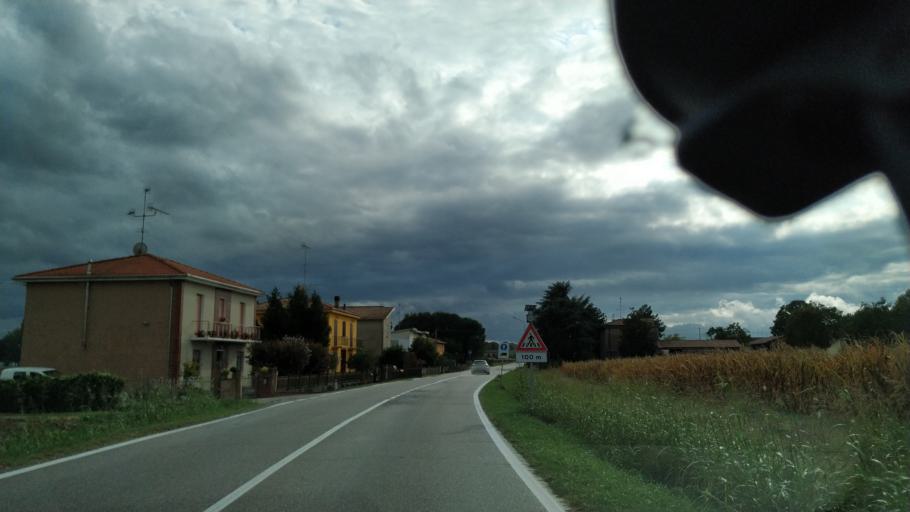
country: IT
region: Emilia-Romagna
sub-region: Provincia di Ferrara
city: San Carlo
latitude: 44.7955
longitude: 11.3994
